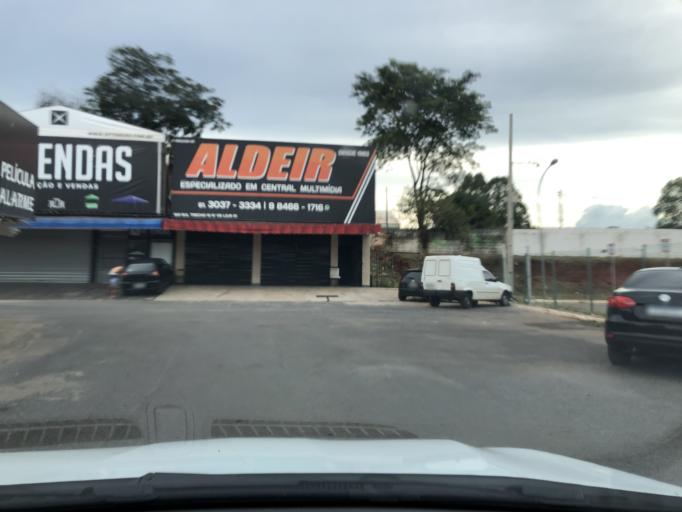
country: BR
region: Federal District
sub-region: Brasilia
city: Brasilia
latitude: -15.7949
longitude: -47.9513
